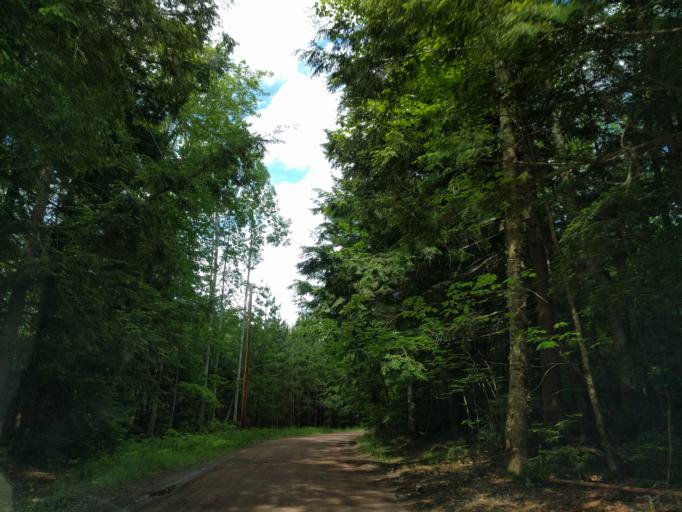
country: US
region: Michigan
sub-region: Marquette County
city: Gwinn
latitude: 46.2592
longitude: -87.3626
